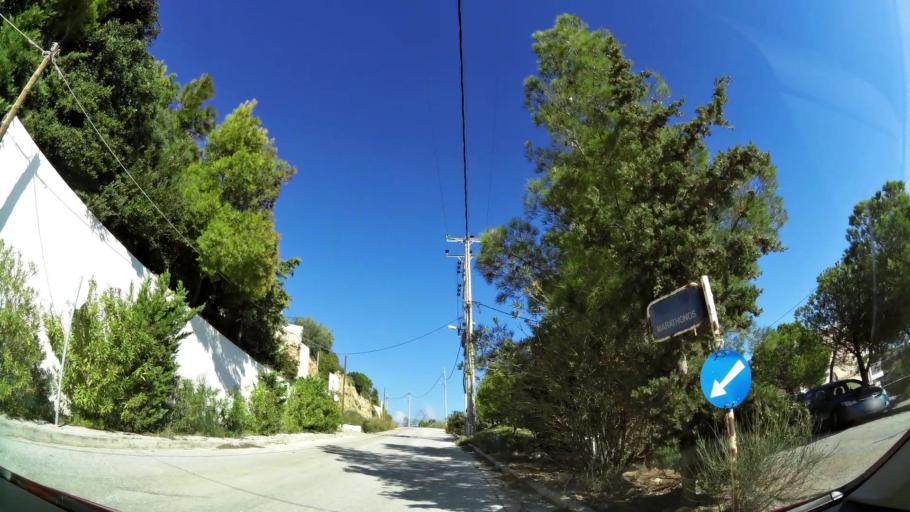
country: GR
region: Attica
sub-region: Nomarchia Anatolikis Attikis
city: Dhrafi
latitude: 38.0206
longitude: 23.8985
